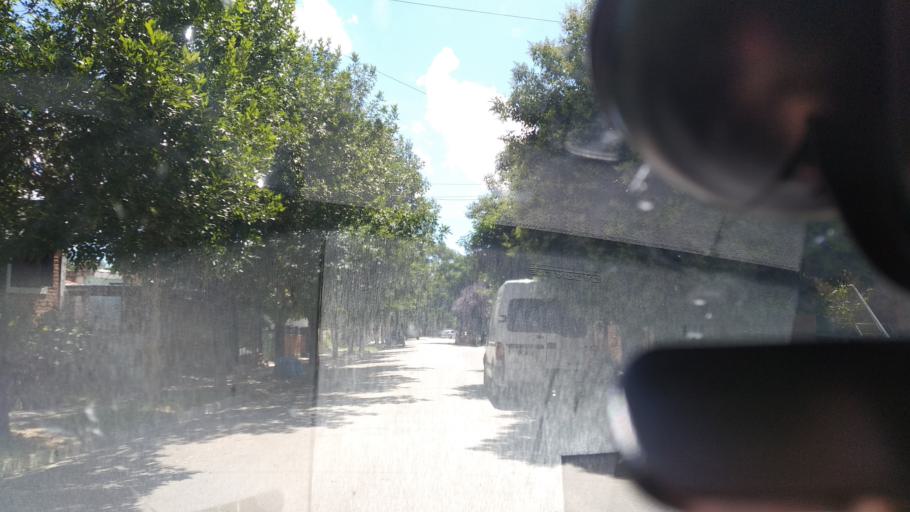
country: AR
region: Cordoba
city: Mina Clavero
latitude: -31.7241
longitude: -65.0111
